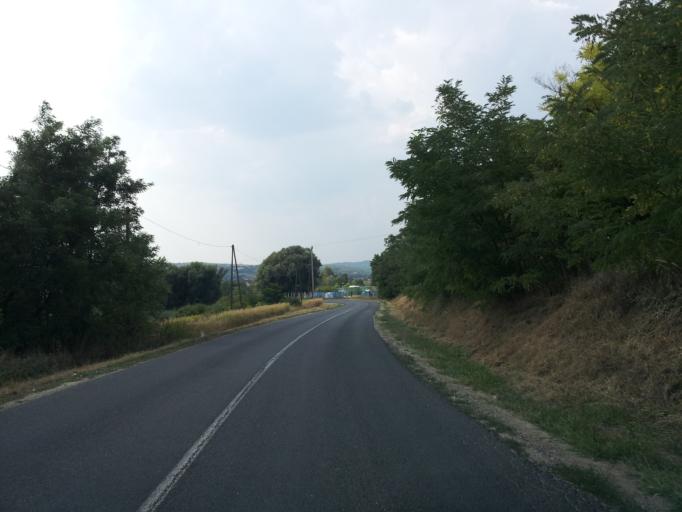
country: HU
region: Gyor-Moson-Sopron
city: Pannonhalma
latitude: 47.5607
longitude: 17.7251
